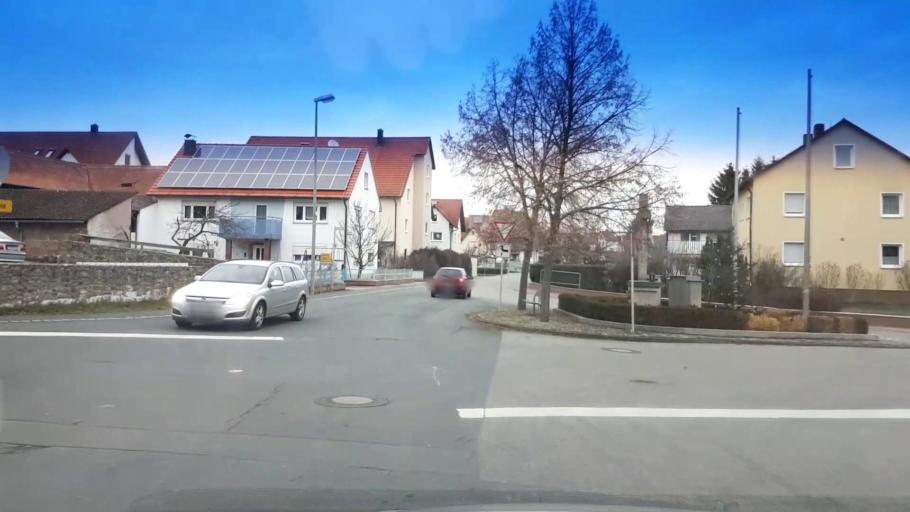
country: DE
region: Bavaria
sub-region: Upper Franconia
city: Hallerndorf
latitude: 49.7736
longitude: 11.0000
